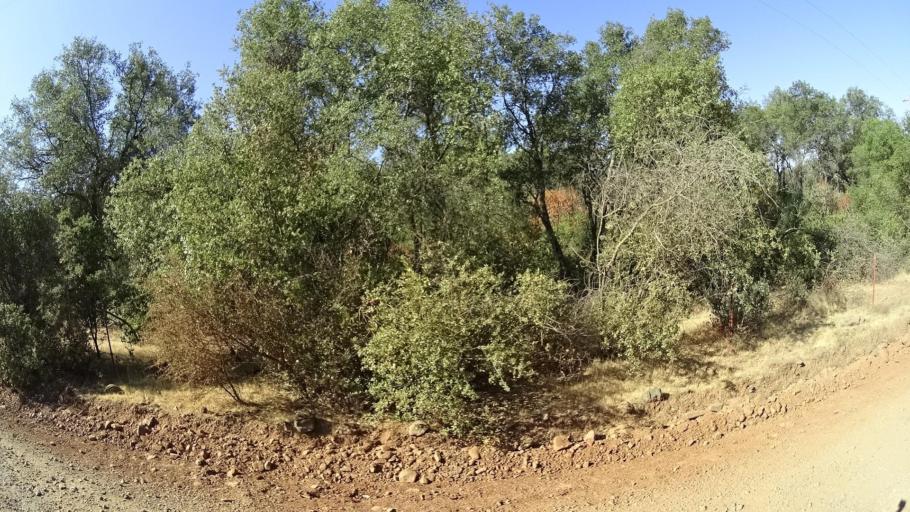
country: US
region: California
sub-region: Mariposa County
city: Mariposa
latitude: 37.6177
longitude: -120.2263
